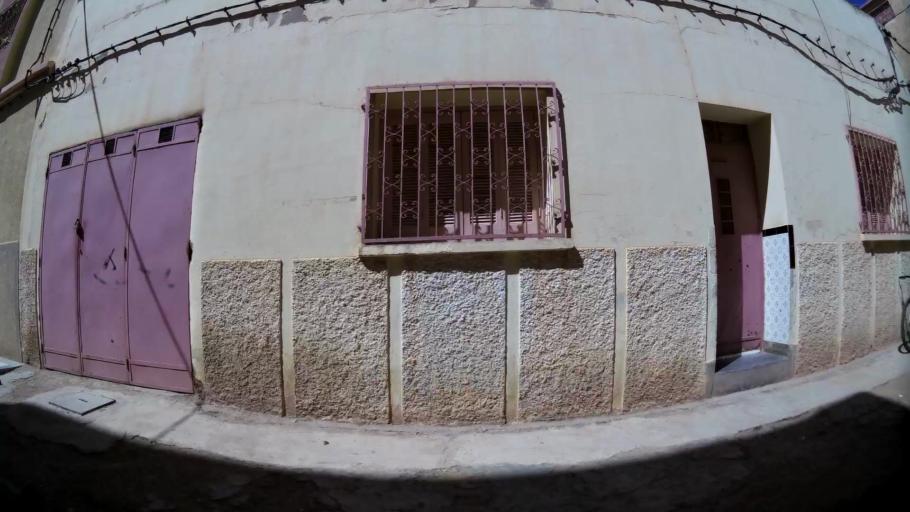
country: MA
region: Oriental
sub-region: Oujda-Angad
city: Oujda
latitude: 34.6688
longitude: -1.9307
